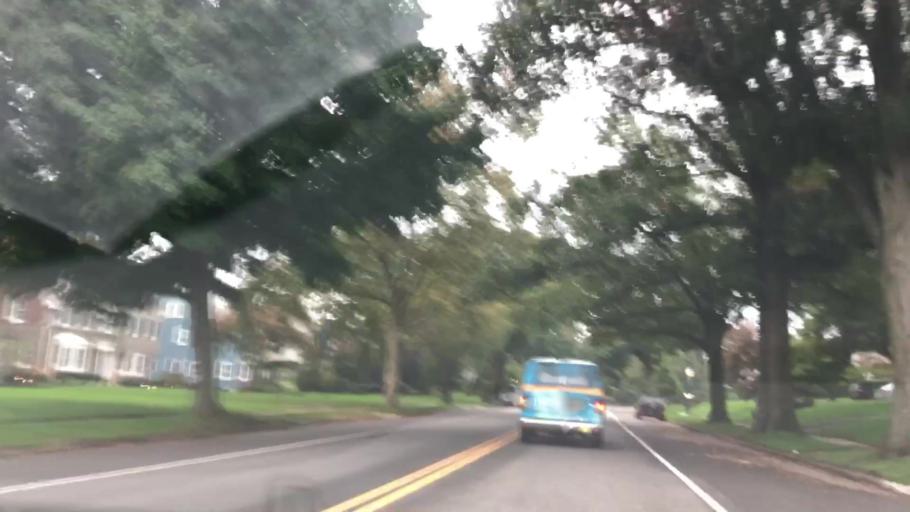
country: US
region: New Jersey
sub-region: Essex County
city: Montclair
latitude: 40.8196
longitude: -74.1978
